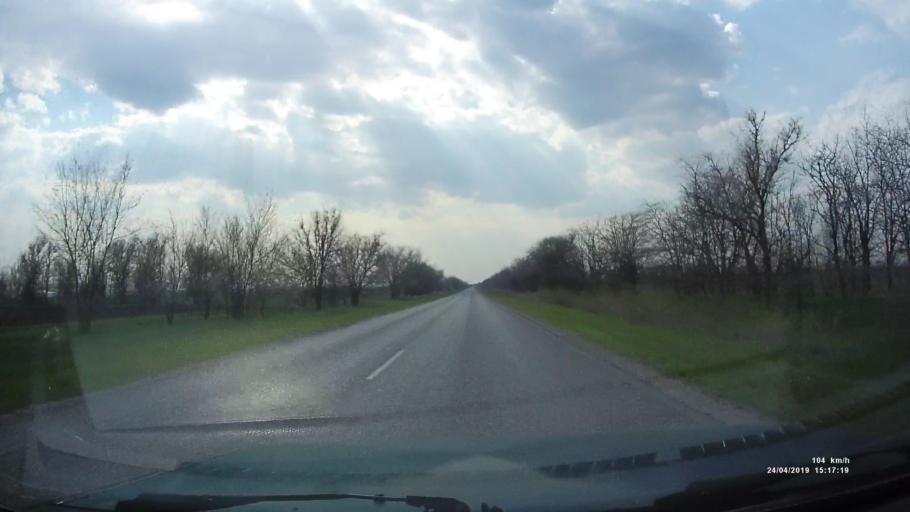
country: RU
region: Rostov
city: Remontnoye
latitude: 46.5465
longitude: 43.1924
